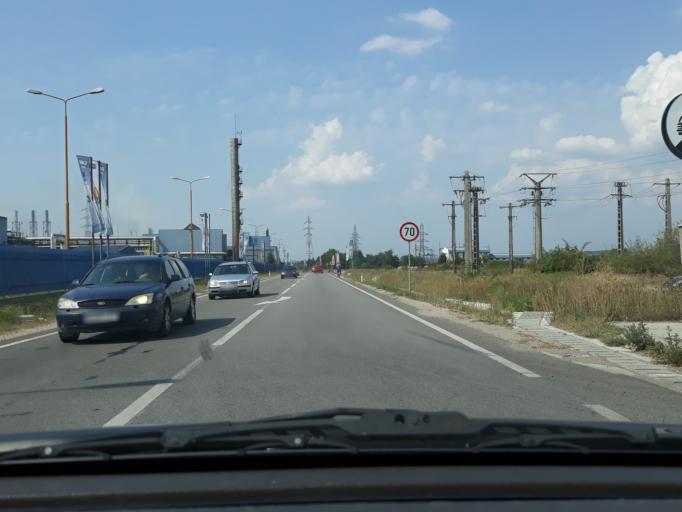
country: RO
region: Bihor
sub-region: Comuna Lazuri de Beius
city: Lazuri de Beius
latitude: 46.6094
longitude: 22.4164
